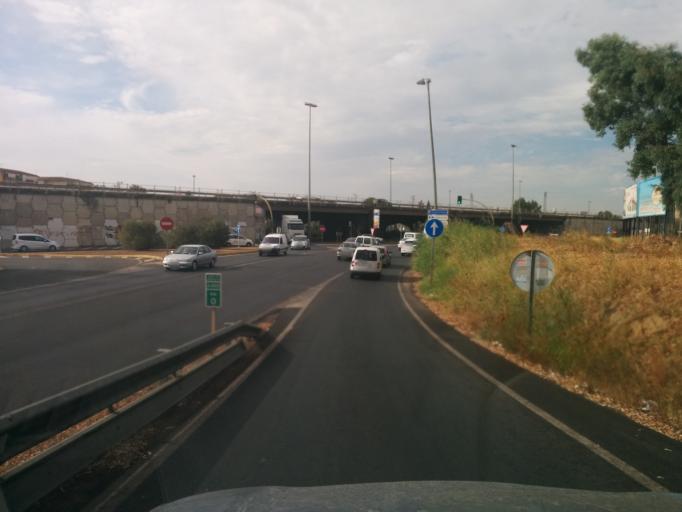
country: ES
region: Andalusia
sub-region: Provincia de Sevilla
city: Sevilla
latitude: 37.4150
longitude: -5.9304
